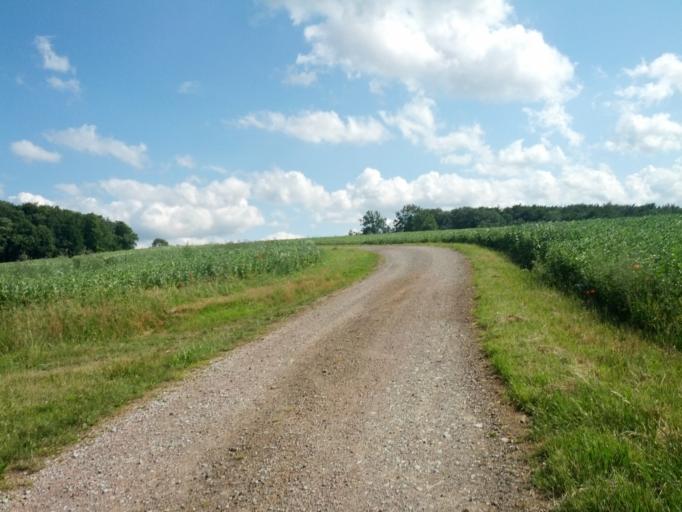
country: DE
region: Thuringia
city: Wolfsburg-Unkeroda
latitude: 50.9719
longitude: 10.2338
